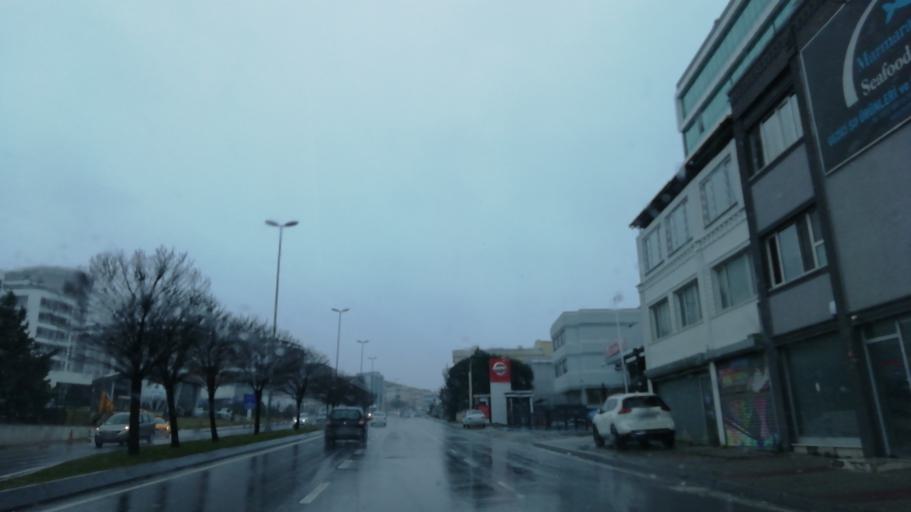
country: TR
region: Istanbul
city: Yakuplu
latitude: 40.9950
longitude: 28.7156
